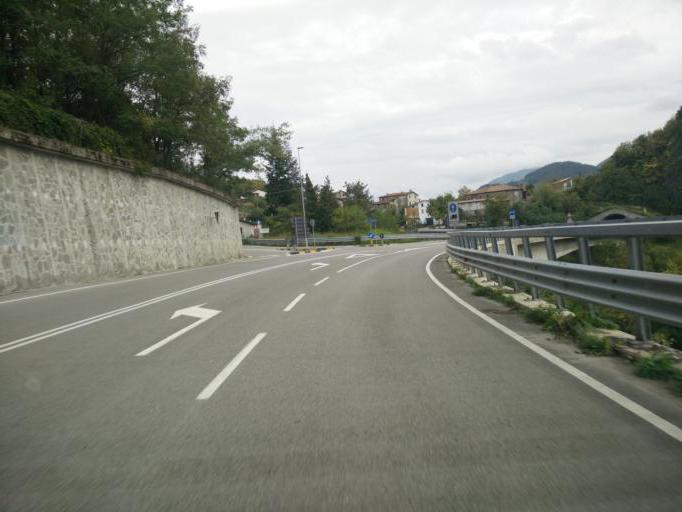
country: IT
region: Tuscany
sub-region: Provincia di Lucca
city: Piazza al Serchio-San Michele
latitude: 44.1834
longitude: 10.3081
